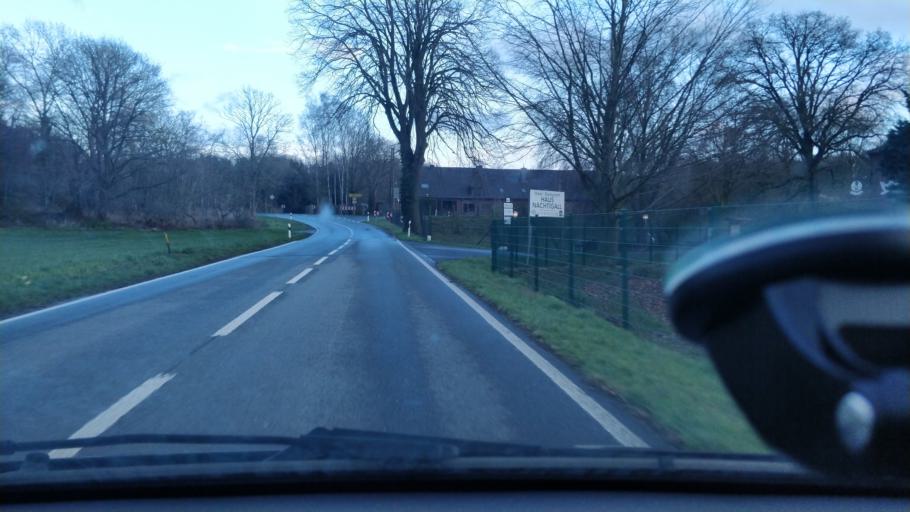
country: DE
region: North Rhine-Westphalia
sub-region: Regierungsbezirk Dusseldorf
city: Uedem
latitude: 51.6796
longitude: 6.3349
